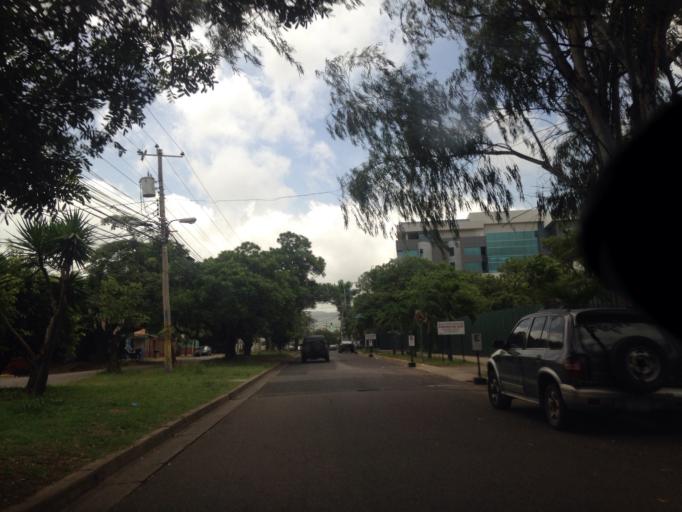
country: HN
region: Francisco Morazan
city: Tegucigalpa
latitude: 14.0785
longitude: -87.1881
